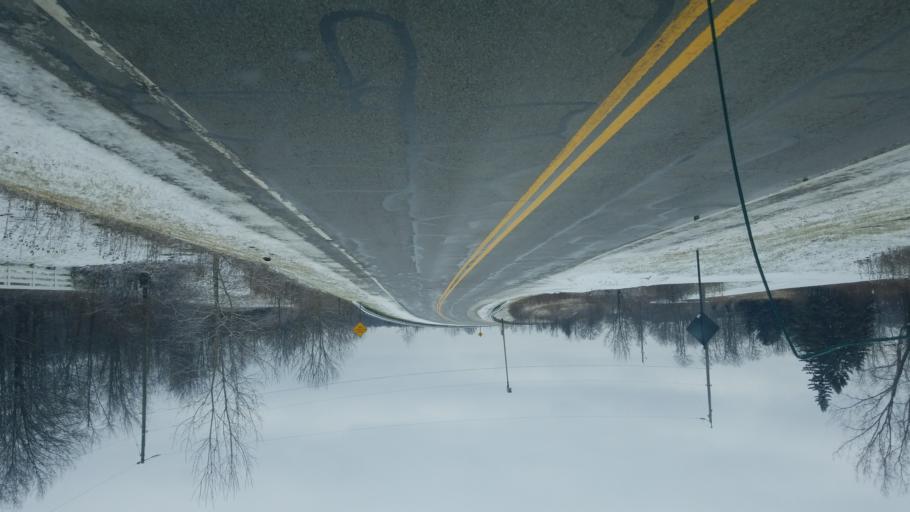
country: US
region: Ohio
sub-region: Franklin County
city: New Albany
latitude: 40.0840
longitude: -82.7885
